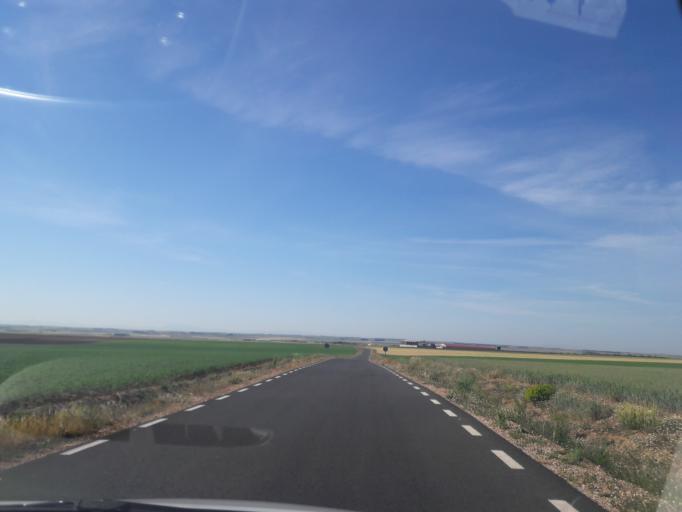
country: ES
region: Castille and Leon
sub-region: Provincia de Salamanca
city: Parada de Rubiales
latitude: 41.1339
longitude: -5.4304
